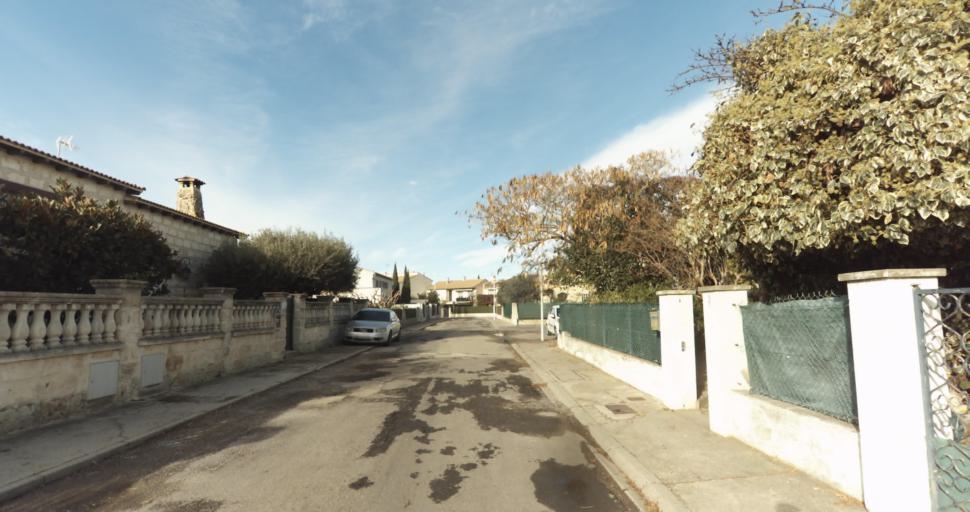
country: FR
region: Languedoc-Roussillon
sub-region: Departement du Gard
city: Aigues-Mortes
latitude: 43.5695
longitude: 4.1962
